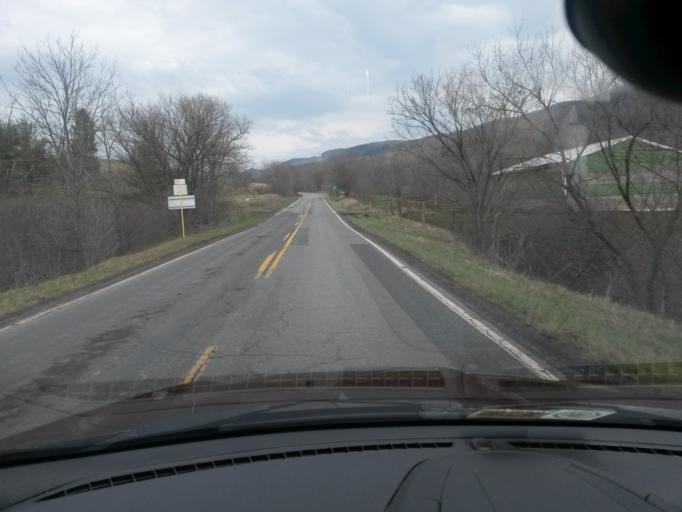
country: US
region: Virginia
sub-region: Highland County
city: Monterey
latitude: 38.2404
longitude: -79.6856
